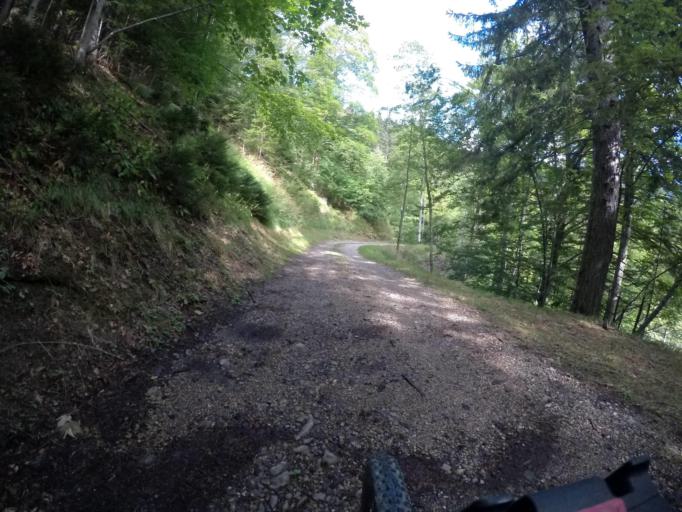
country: IT
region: Friuli Venezia Giulia
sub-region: Provincia di Udine
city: Paularo
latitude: 46.4945
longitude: 13.1859
